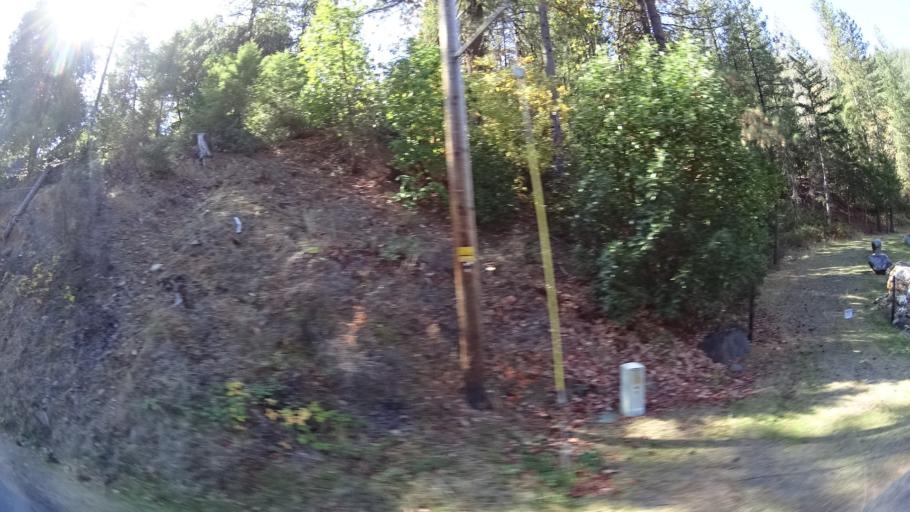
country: US
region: California
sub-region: Siskiyou County
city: Yreka
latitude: 41.7466
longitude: -123.0081
